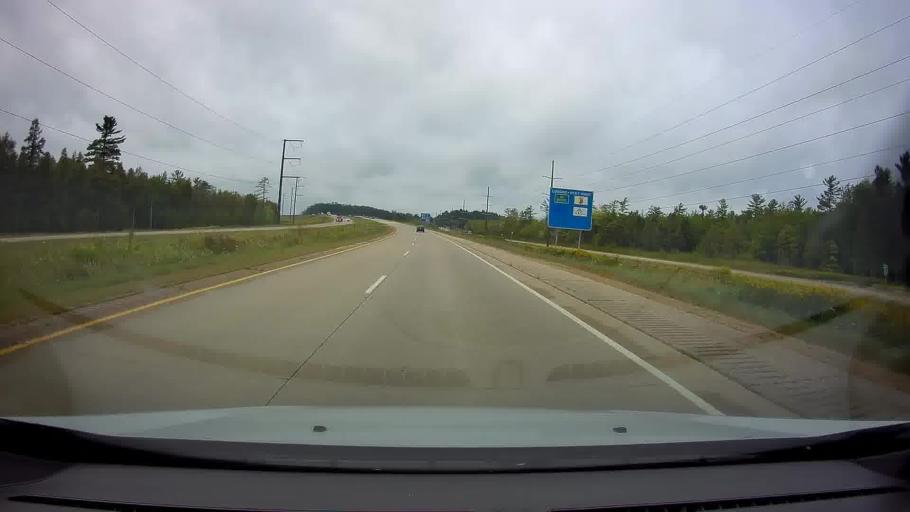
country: US
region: Wisconsin
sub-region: Shawano County
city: Shawano
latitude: 44.7608
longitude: -88.5478
